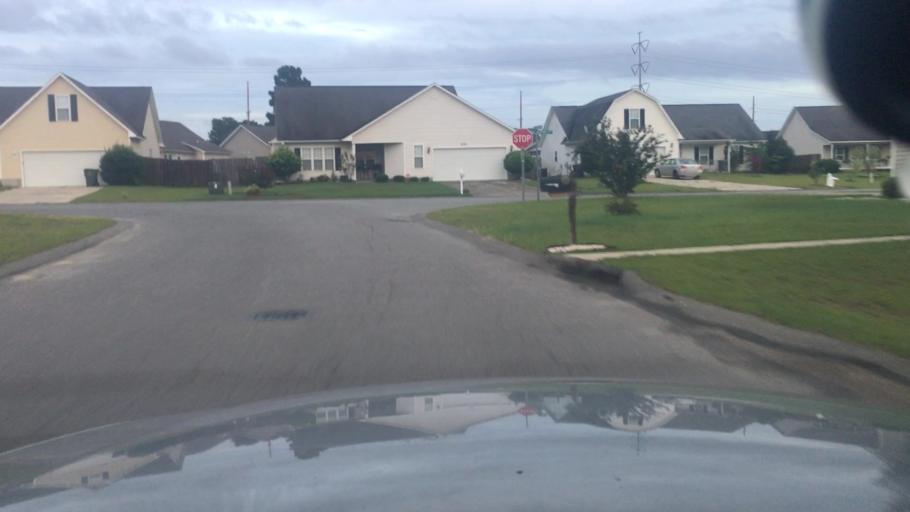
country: US
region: North Carolina
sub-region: Cumberland County
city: Hope Mills
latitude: 34.9847
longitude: -78.9159
